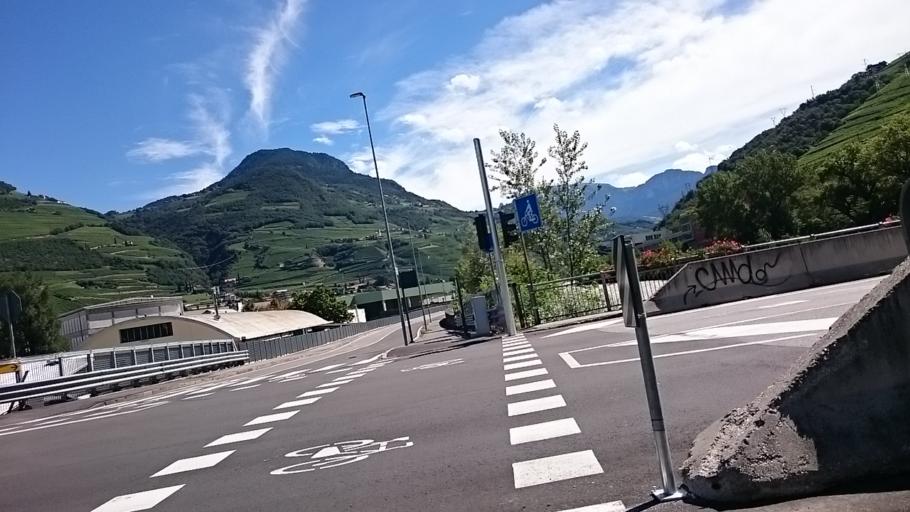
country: IT
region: Trentino-Alto Adige
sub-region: Bolzano
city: Cardano
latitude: 46.4931
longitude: 11.3685
